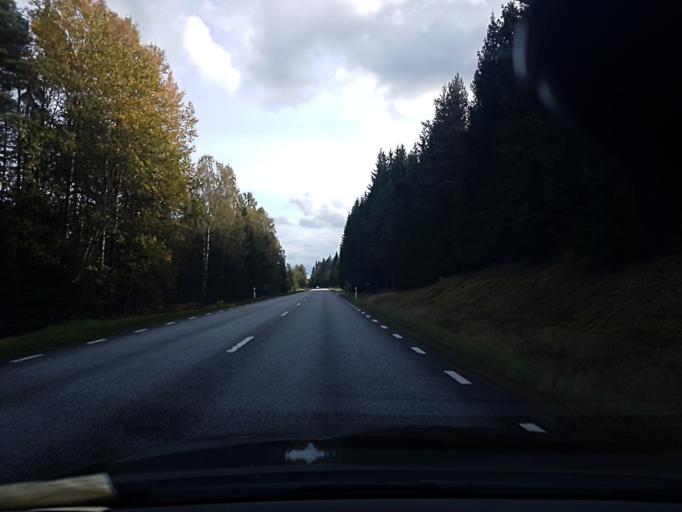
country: SE
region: Joenkoeping
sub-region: Varnamo Kommun
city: Bredaryd
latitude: 57.1933
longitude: 13.7204
